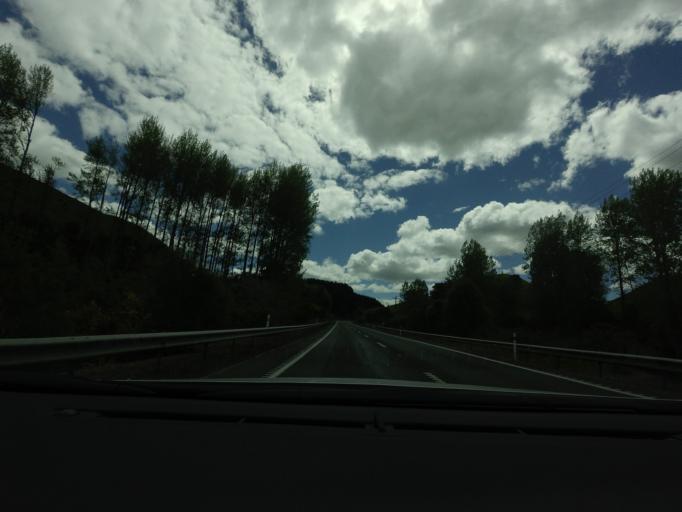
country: NZ
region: Bay of Plenty
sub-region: Rotorua District
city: Rotorua
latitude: -38.2967
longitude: 176.3595
